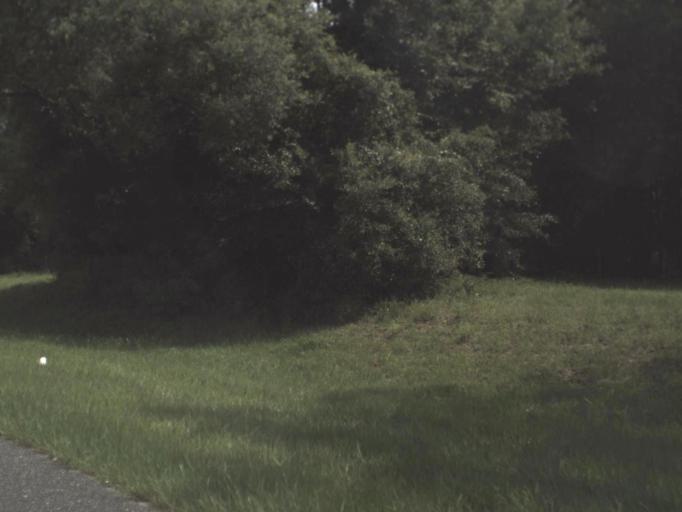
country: US
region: Florida
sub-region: Alachua County
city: High Springs
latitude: 29.8629
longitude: -82.6086
